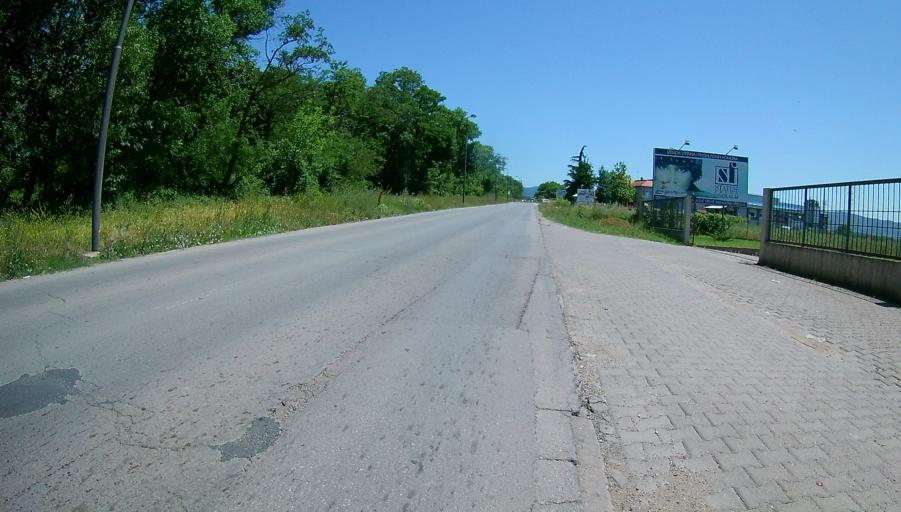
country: RS
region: Central Serbia
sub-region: Nisavski Okrug
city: Nis
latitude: 43.3012
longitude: 21.8735
